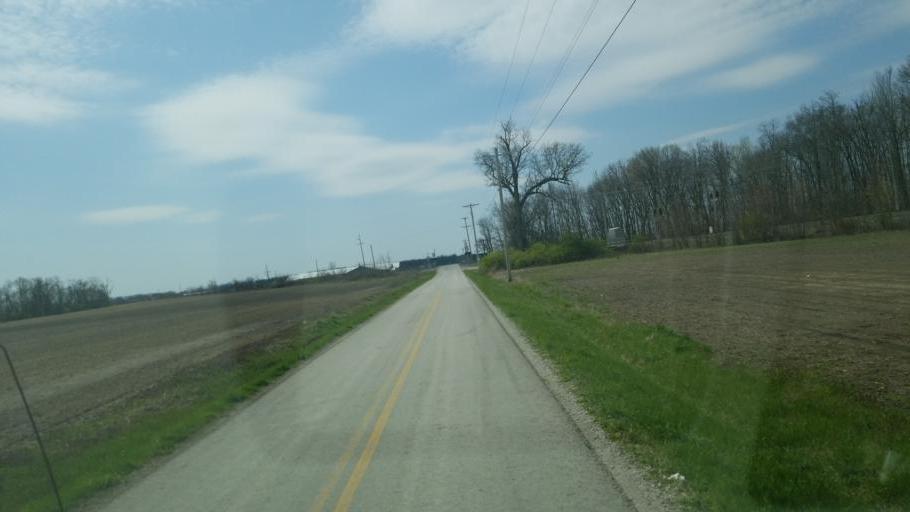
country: US
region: Ohio
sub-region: Delaware County
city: Delaware
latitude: 40.3657
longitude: -83.1206
